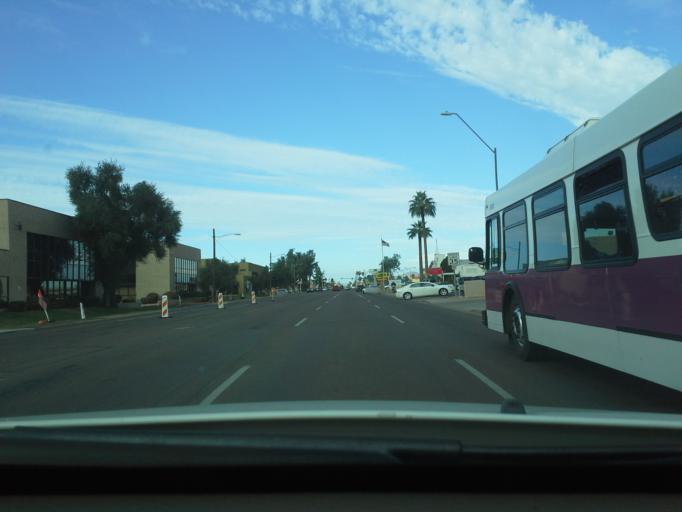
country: US
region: Arizona
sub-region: Maricopa County
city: Phoenix
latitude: 33.4845
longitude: -112.0999
